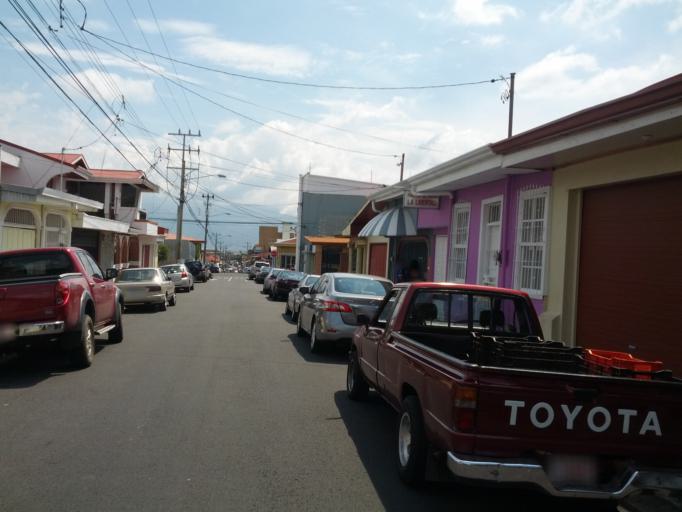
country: CR
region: Alajuela
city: Alajuela
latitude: 10.0194
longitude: -84.2106
